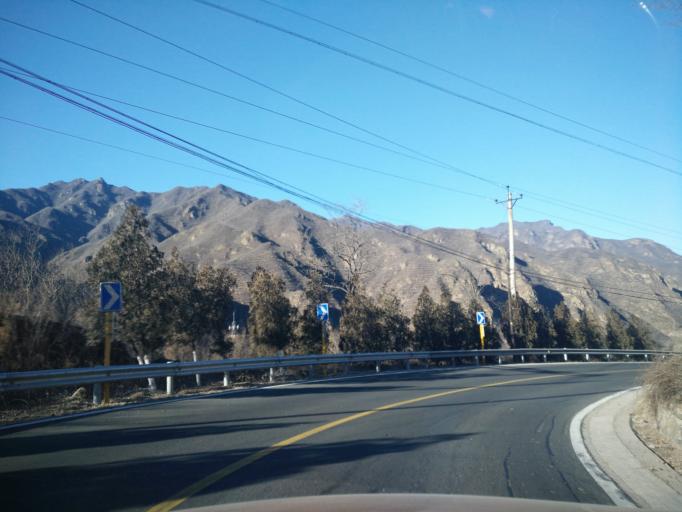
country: CN
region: Beijing
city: Wangping
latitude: 40.0032
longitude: 115.9435
